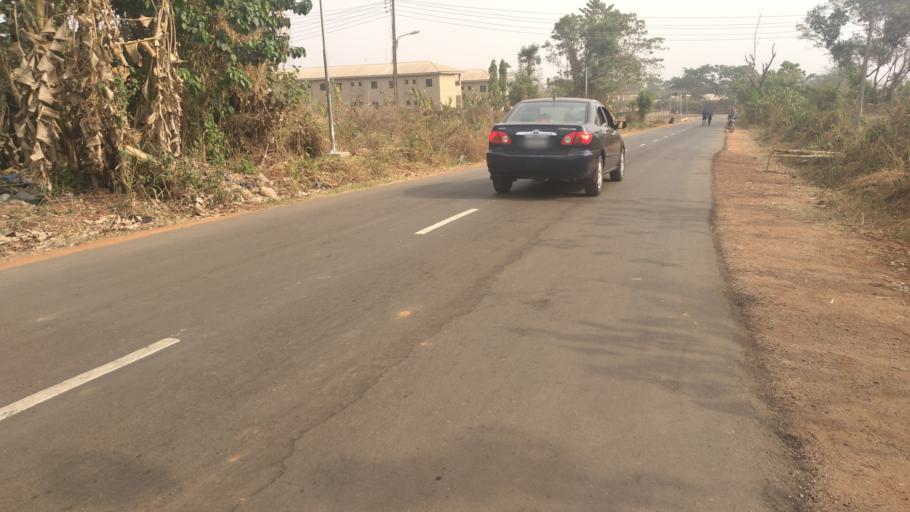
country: NG
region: Ondo
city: Ilare
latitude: 7.2987
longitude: 5.1453
